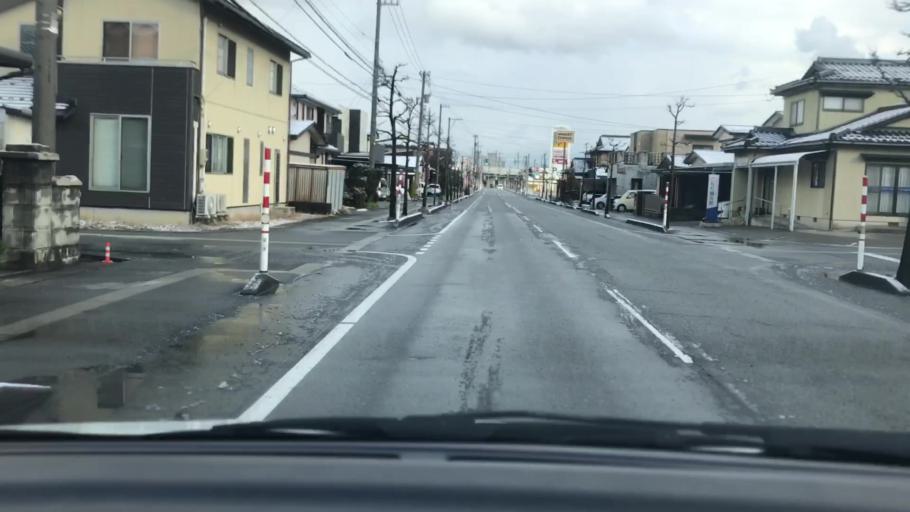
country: JP
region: Toyama
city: Toyama-shi
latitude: 36.7075
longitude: 137.2389
